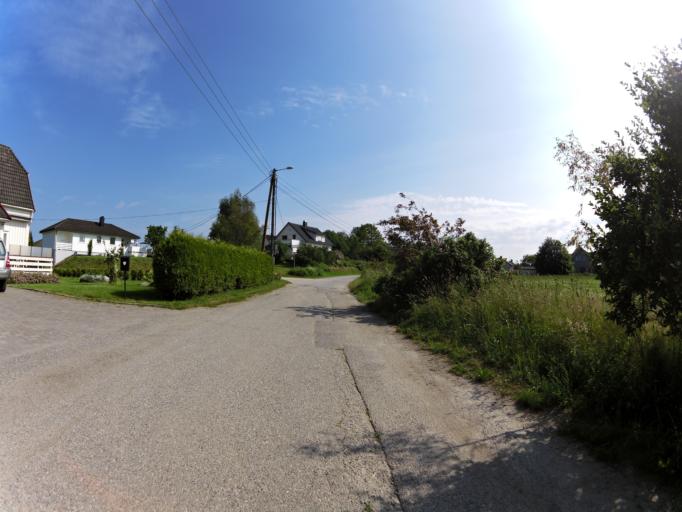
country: NO
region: Ostfold
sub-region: Sarpsborg
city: Sarpsborg
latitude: 59.2645
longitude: 11.0214
